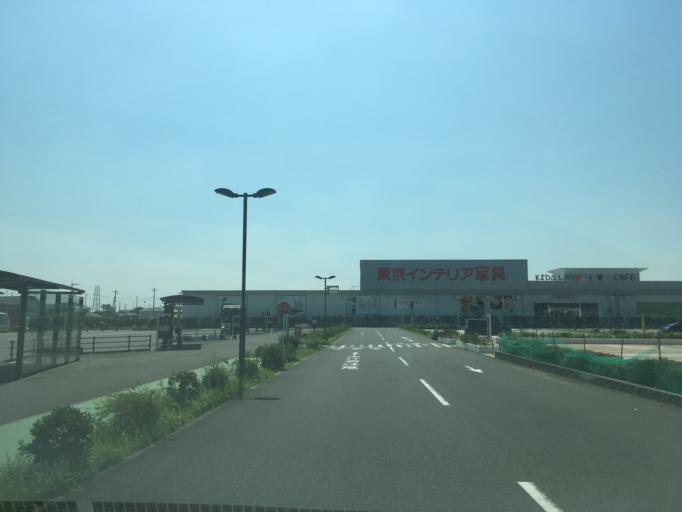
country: JP
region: Chiba
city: Kisarazu
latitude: 35.4345
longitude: 139.9378
